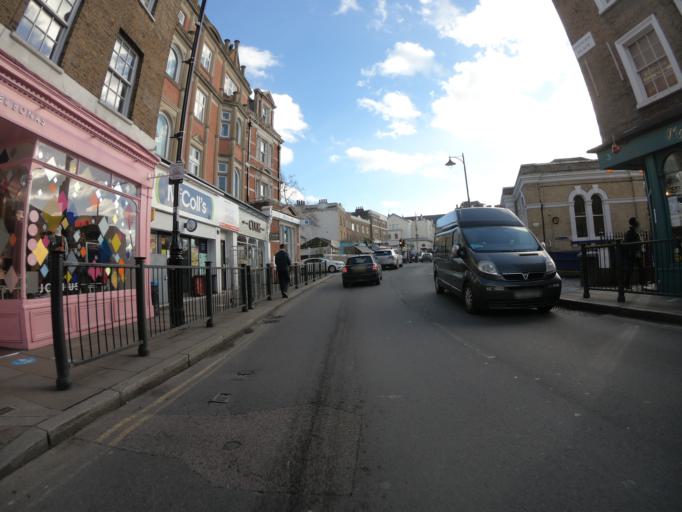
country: GB
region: England
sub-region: Greater London
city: Blackheath
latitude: 51.4660
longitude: 0.0089
